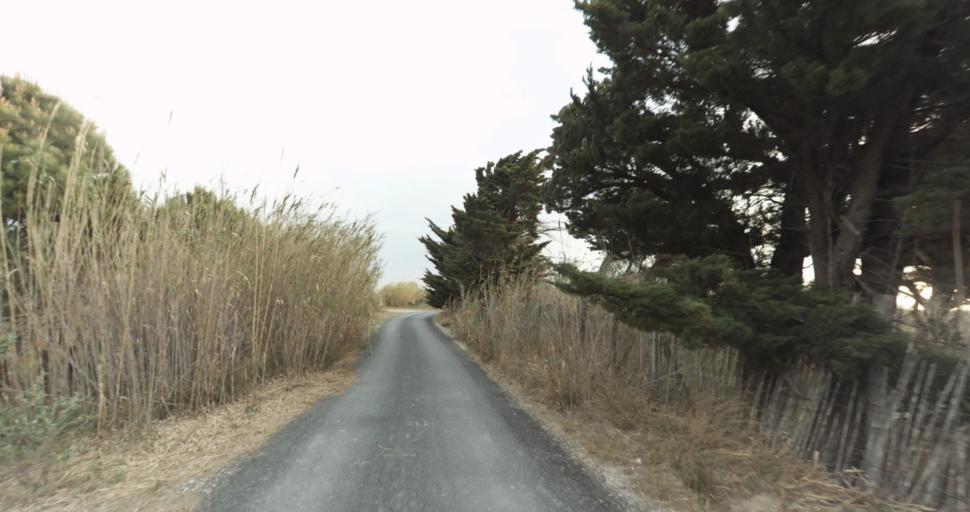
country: FR
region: Languedoc-Roussillon
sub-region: Departement de l'Aude
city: Leucate
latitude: 42.9479
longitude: 3.0300
